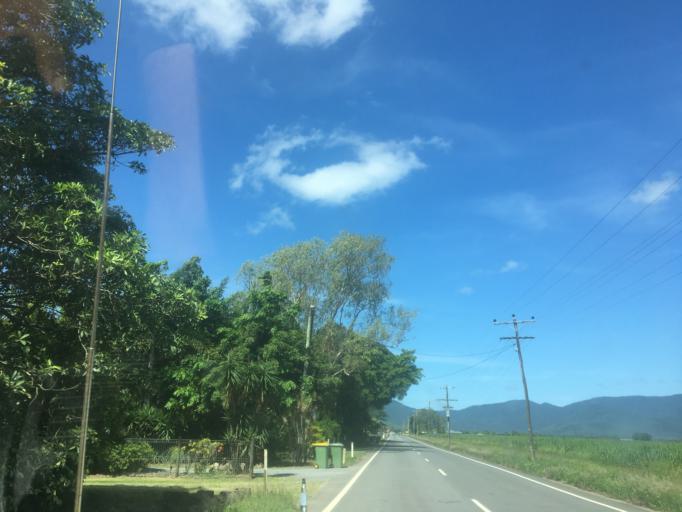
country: AU
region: Queensland
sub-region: Cairns
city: Woree
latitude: -17.0628
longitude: 145.7590
